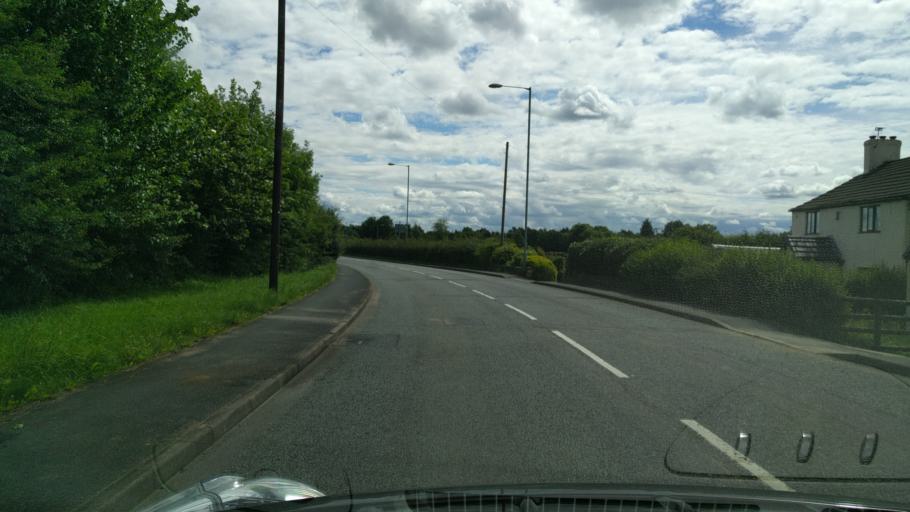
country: GB
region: England
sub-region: Warrington
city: Culcheth
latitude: 53.4364
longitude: -2.5269
